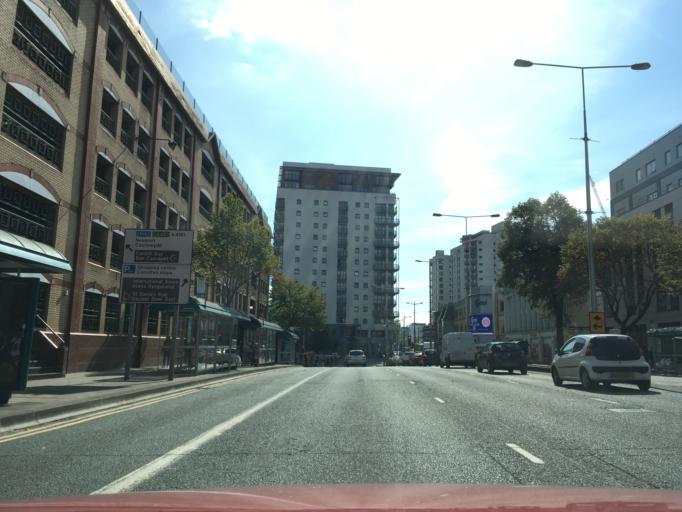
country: GB
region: Wales
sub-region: Cardiff
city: Cardiff
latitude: 51.4841
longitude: -3.1719
